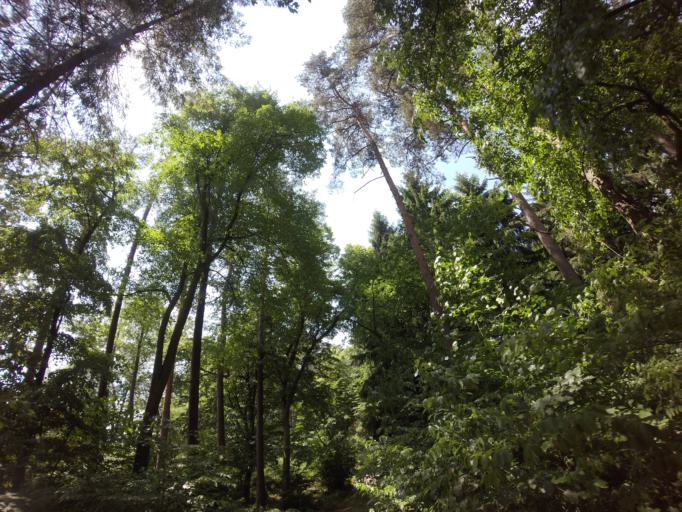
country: PL
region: West Pomeranian Voivodeship
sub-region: Powiat choszczenski
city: Bierzwnik
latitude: 53.0825
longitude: 15.7022
